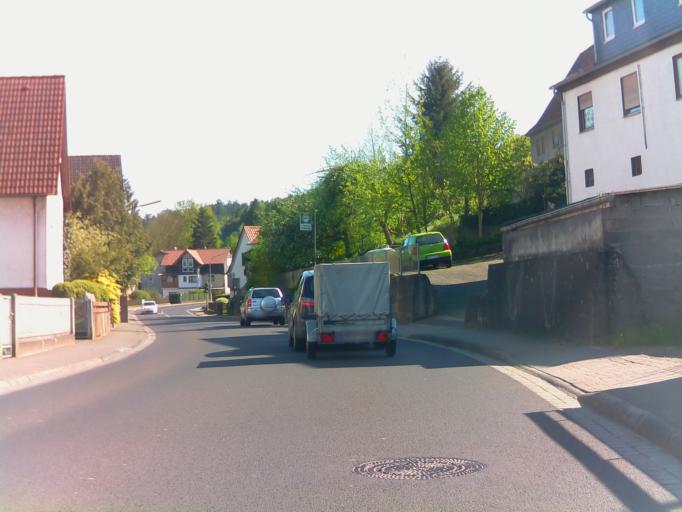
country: DE
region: Hesse
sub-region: Regierungsbezirk Darmstadt
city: Wachtersbach
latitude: 50.3004
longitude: 9.2997
